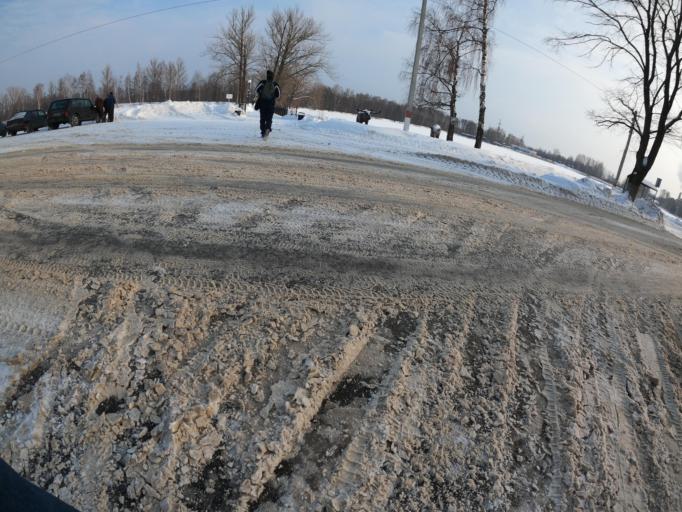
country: RU
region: Moskovskaya
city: Elektrogorsk
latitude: 55.8935
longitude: 38.7773
